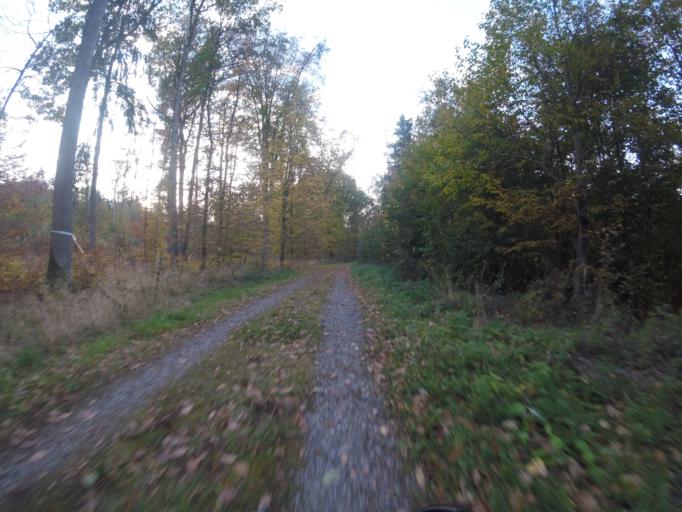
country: DE
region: Baden-Wuerttemberg
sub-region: Regierungsbezirk Stuttgart
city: Kirchberg an der Murr
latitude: 48.9804
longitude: 9.3505
